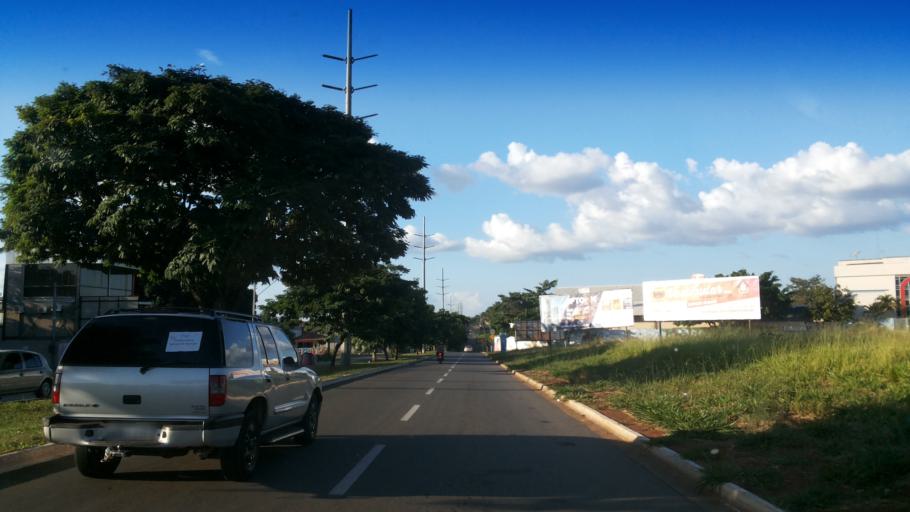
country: BR
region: Goias
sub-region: Goiania
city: Goiania
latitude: -16.7412
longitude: -49.3144
